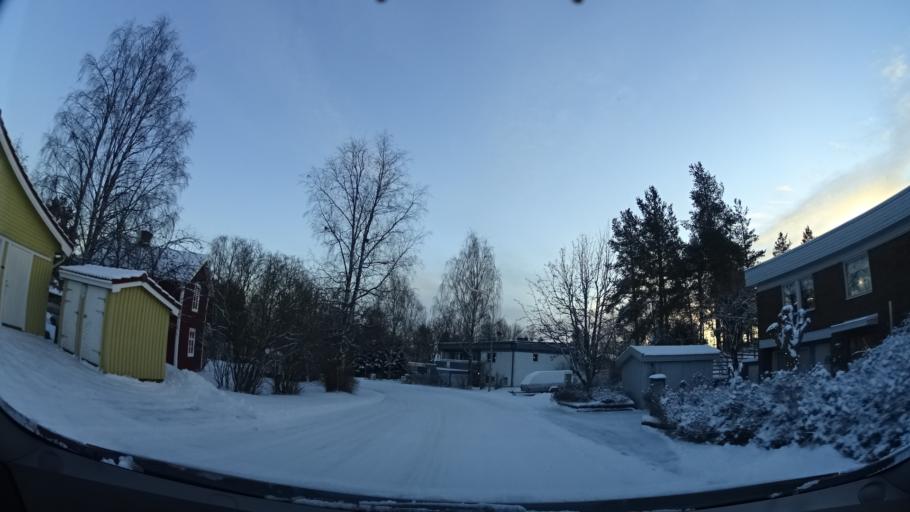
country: SE
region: Vaesterbotten
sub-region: Skelleftea Kommun
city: Kage
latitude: 64.8414
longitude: 20.9835
